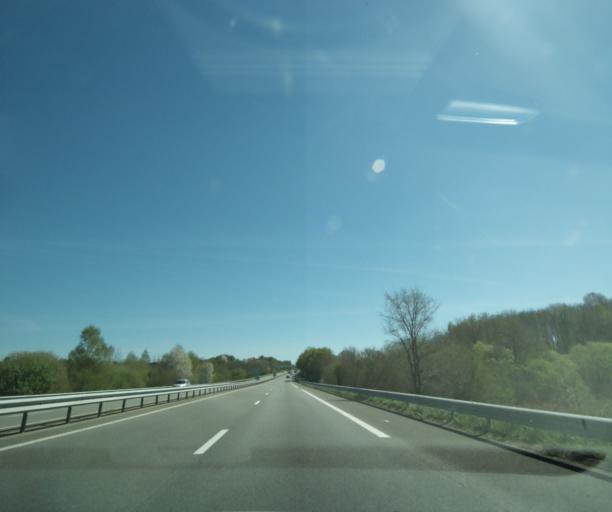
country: FR
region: Limousin
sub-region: Departement de la Haute-Vienne
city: Vicq-sur-Breuilh
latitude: 45.6321
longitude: 1.4314
